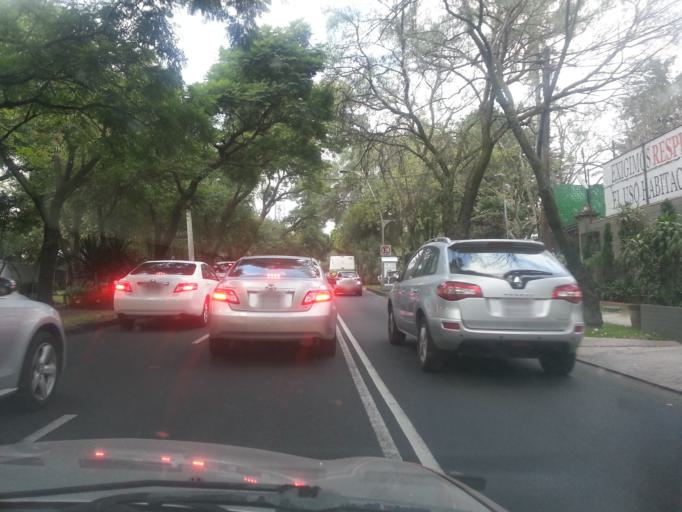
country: MX
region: Mexico City
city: Polanco
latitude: 19.4145
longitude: -99.2195
